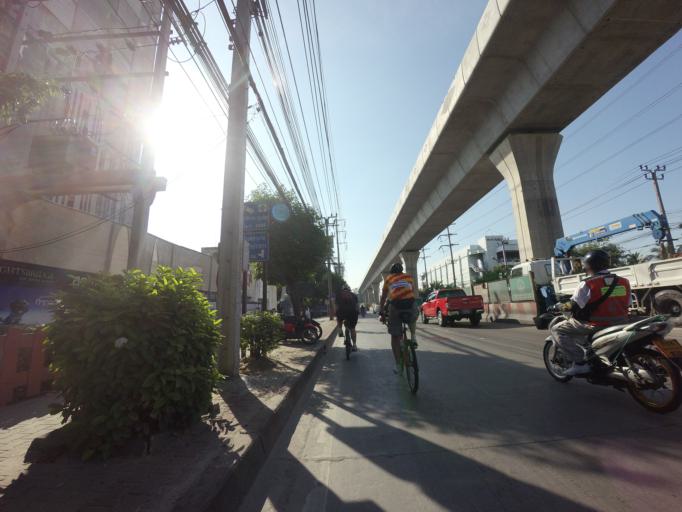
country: TH
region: Samut Prakan
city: Samut Prakan
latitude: 13.6051
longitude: 100.5963
